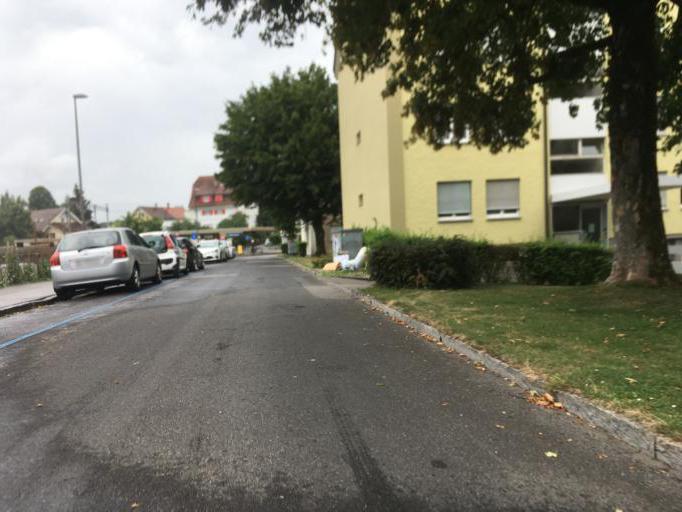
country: CH
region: Bern
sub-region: Bern-Mittelland District
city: Koniz
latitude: 46.9472
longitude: 7.4006
